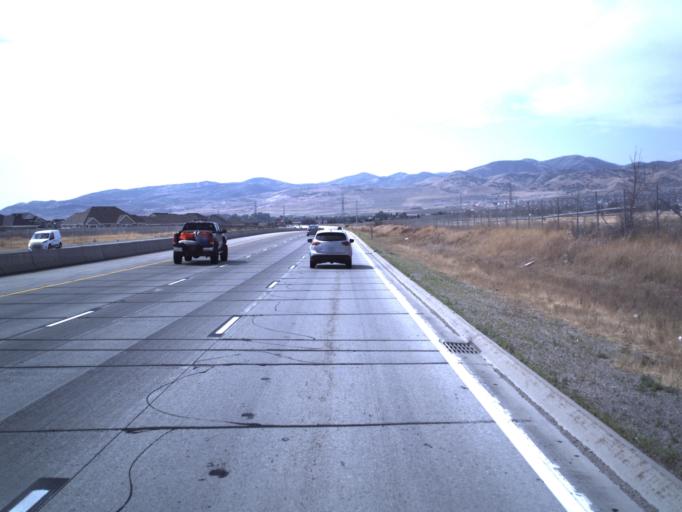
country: US
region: Utah
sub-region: Salt Lake County
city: Riverton
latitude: 40.5189
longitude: -111.9843
